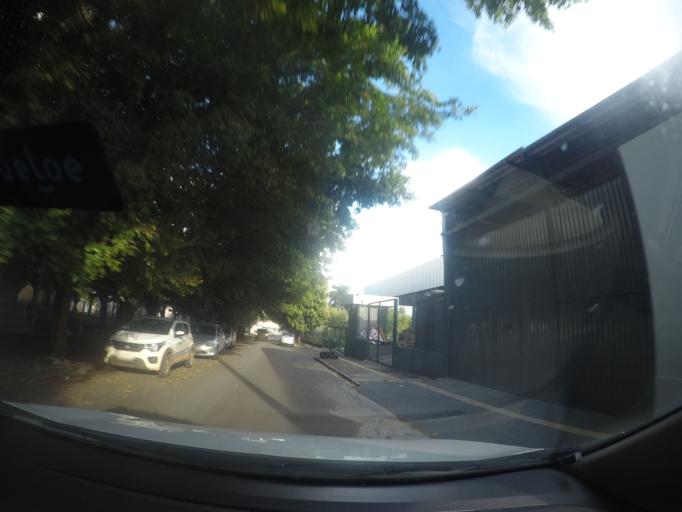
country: BR
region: Goias
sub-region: Goiania
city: Goiania
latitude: -16.6718
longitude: -49.3010
